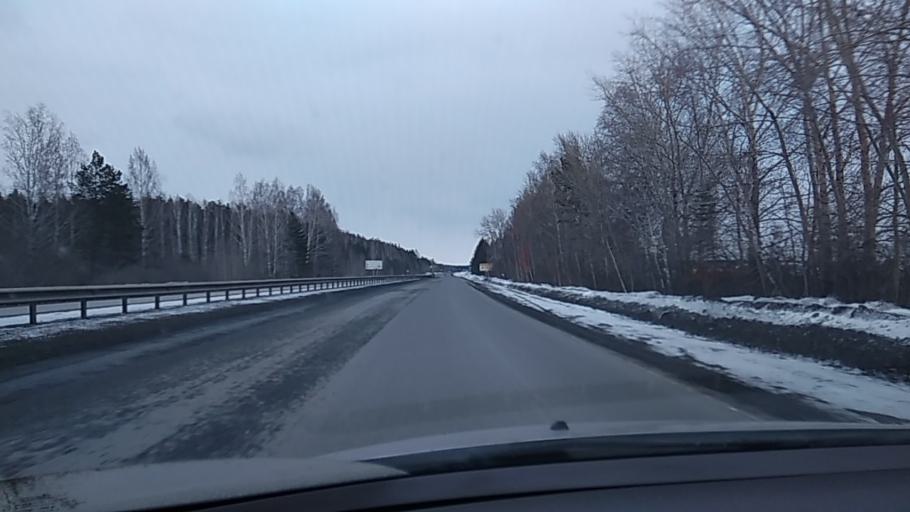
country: RU
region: Sverdlovsk
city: Verkhneye Dubrovo
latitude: 56.7296
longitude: 61.0317
